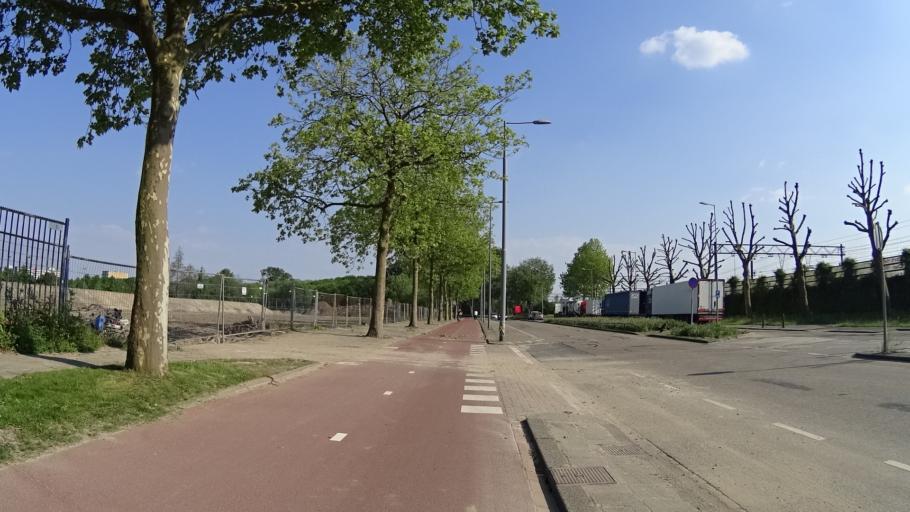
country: NL
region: South Holland
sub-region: Gemeente Barendrecht
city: Barendrecht
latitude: 51.8888
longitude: 4.5247
